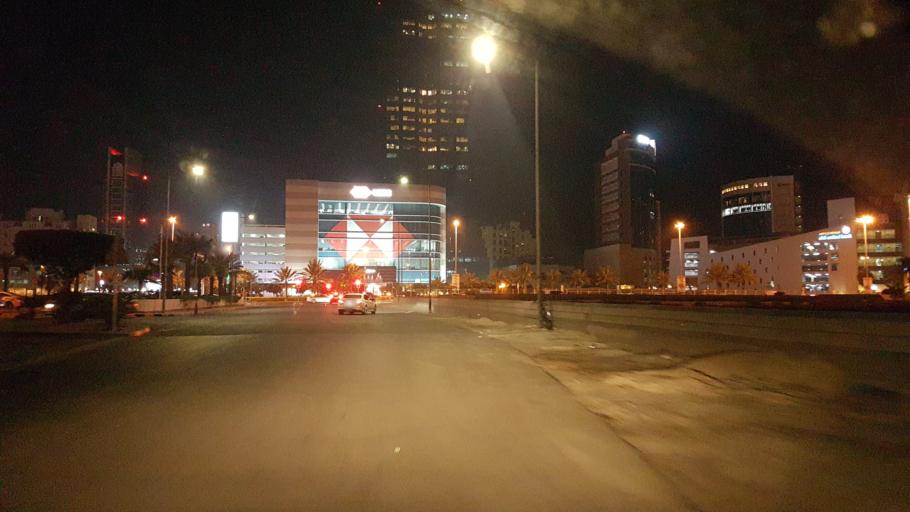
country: BH
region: Manama
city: Jidd Hafs
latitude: 26.2334
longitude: 50.5415
